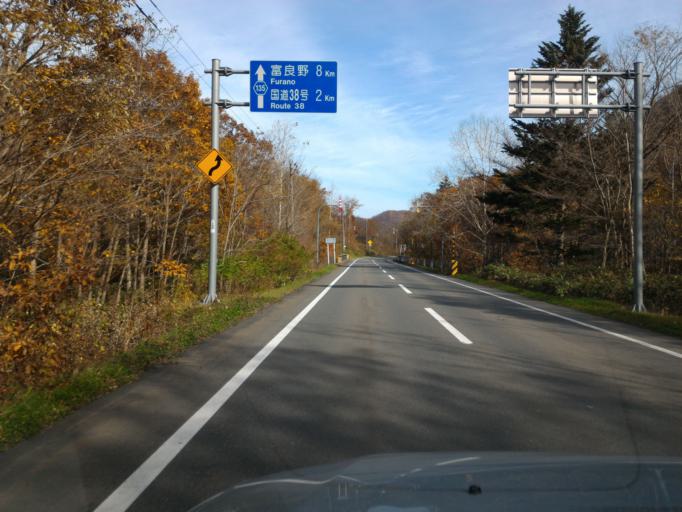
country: JP
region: Hokkaido
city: Shimo-furano
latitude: 43.3684
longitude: 142.3250
